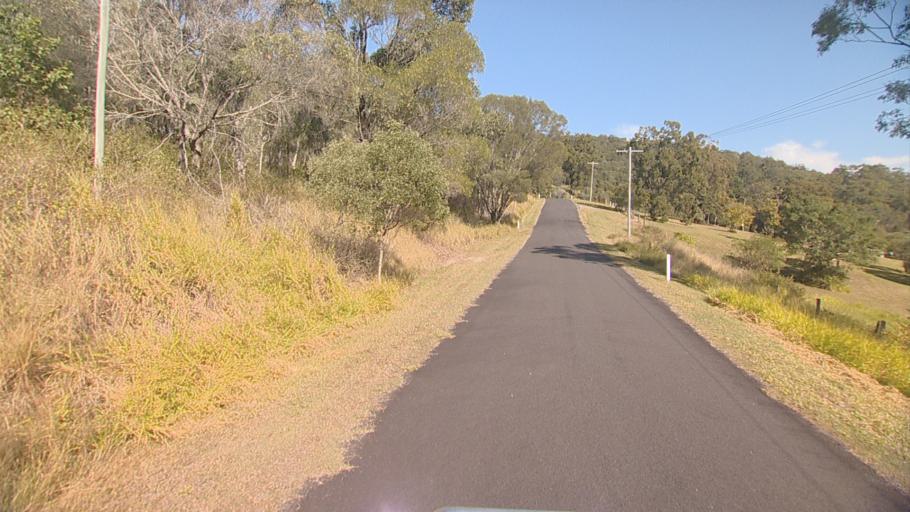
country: AU
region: Queensland
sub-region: Logan
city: Windaroo
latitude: -27.7419
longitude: 153.1729
